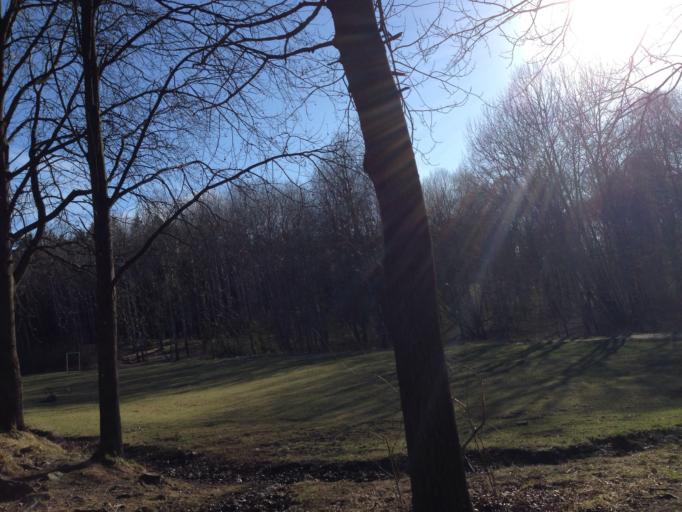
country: SE
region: Stockholm
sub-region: Nacka Kommun
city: Nacka
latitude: 59.2923
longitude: 18.1237
